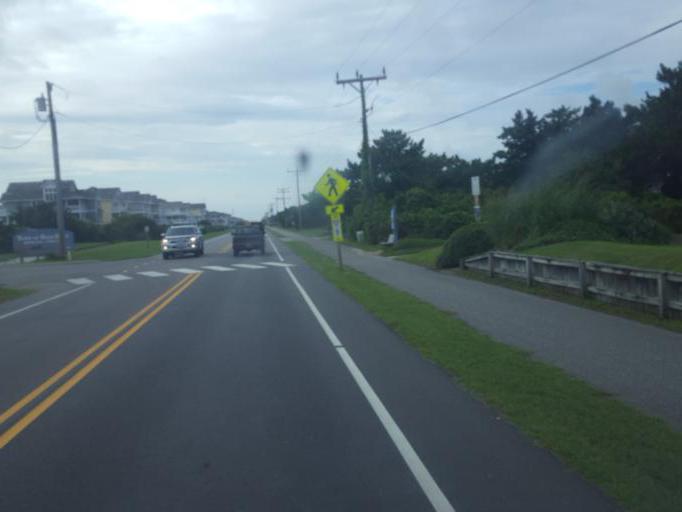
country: US
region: North Carolina
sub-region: Dare County
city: Nags Head
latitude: 35.9342
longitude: -75.6112
